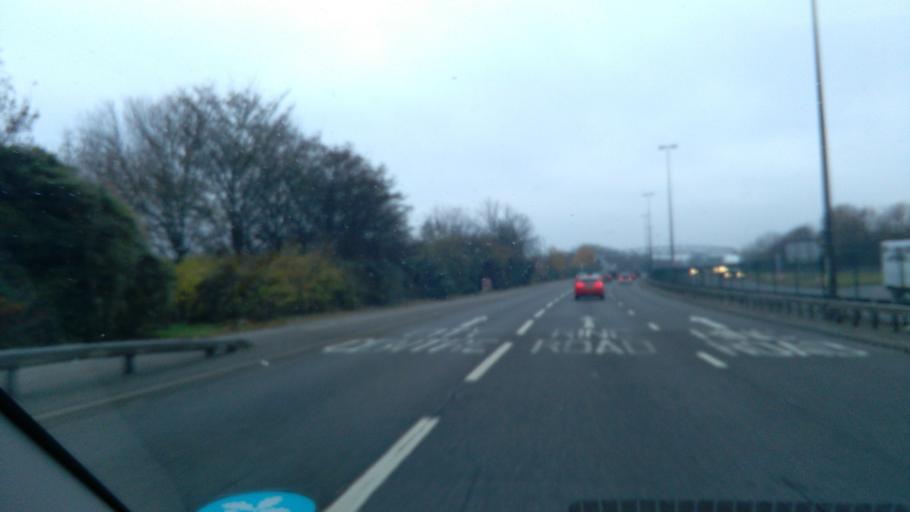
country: GB
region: England
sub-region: Nottingham
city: Nottingham
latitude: 52.9367
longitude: -1.1742
